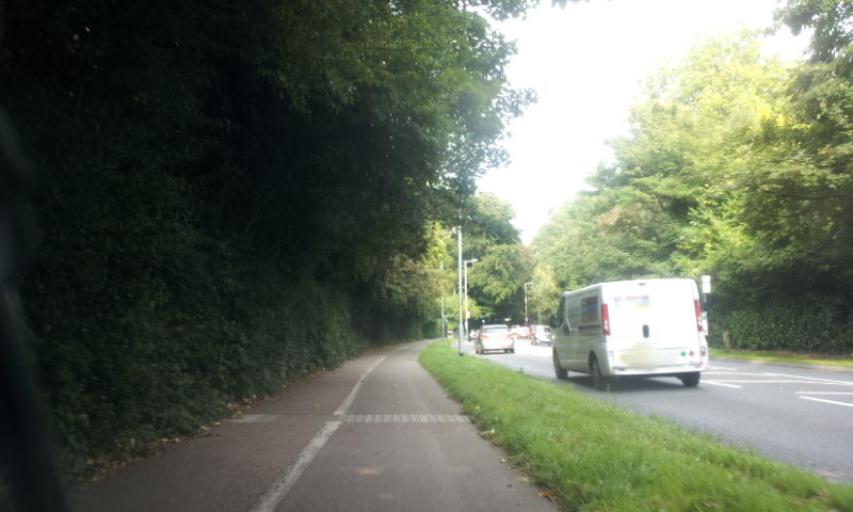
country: GB
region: England
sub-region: Kent
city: Royal Tunbridge Wells
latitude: 51.1374
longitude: 0.2885
